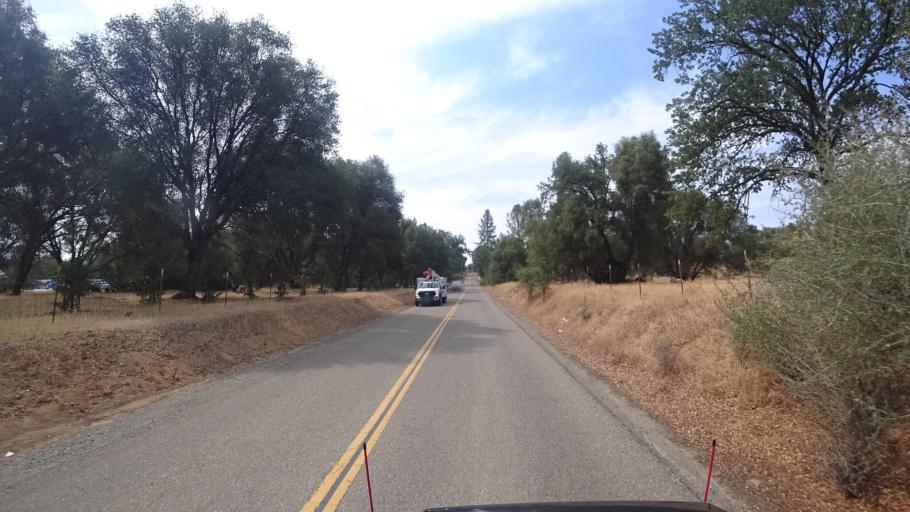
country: US
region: California
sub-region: Mariposa County
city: Mariposa
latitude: 37.4786
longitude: -119.8998
